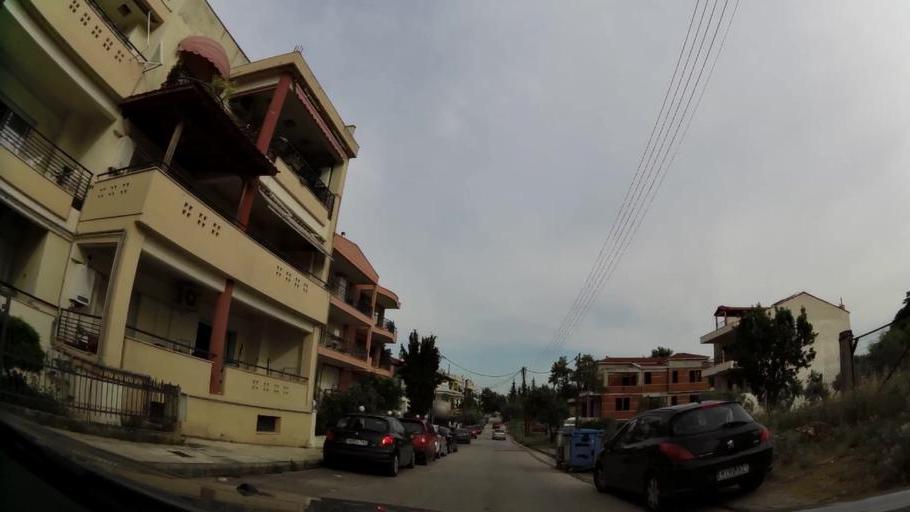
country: GR
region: Central Macedonia
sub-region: Nomos Thessalonikis
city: Thermi
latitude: 40.5511
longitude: 23.0259
